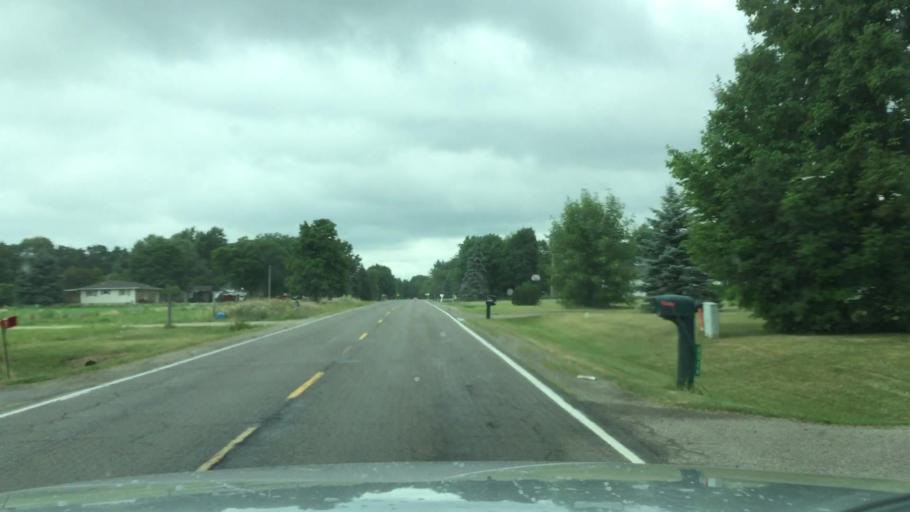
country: US
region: Michigan
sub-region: Genesee County
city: Clio
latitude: 43.1279
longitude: -83.7738
